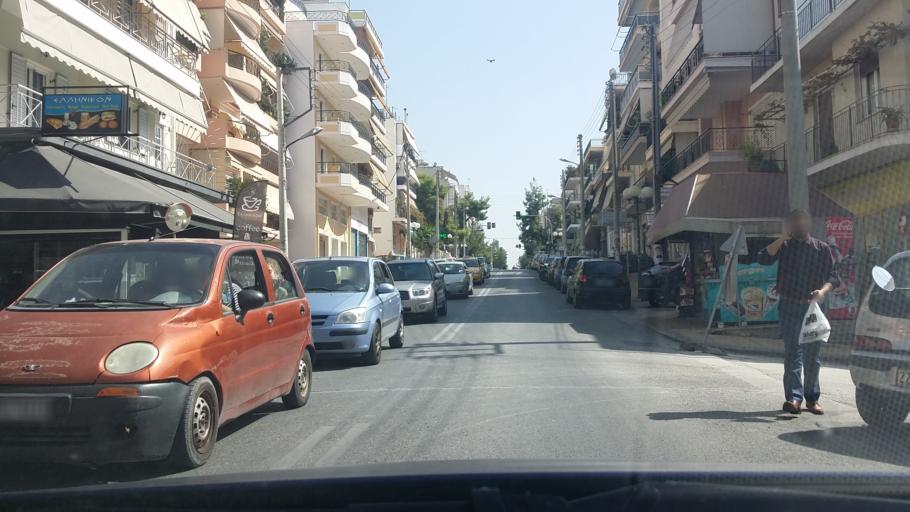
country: GR
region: Attica
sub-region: Nomarchia Athinas
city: Nea Ionia
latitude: 38.0394
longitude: 23.7625
